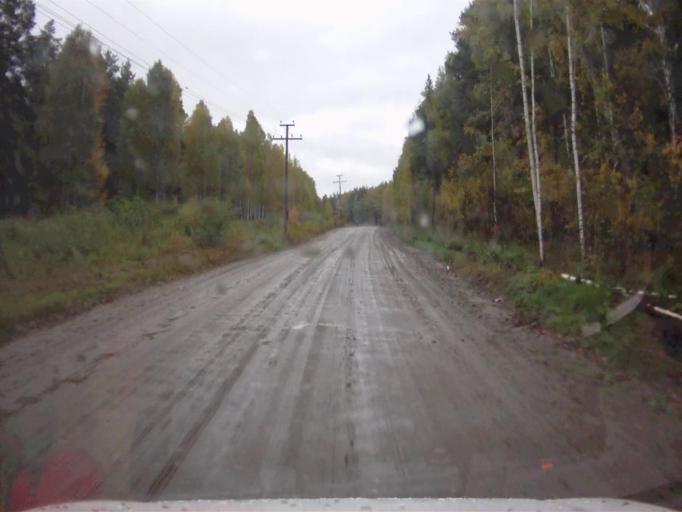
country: RU
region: Chelyabinsk
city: Kyshtym
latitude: 55.8021
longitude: 60.4797
